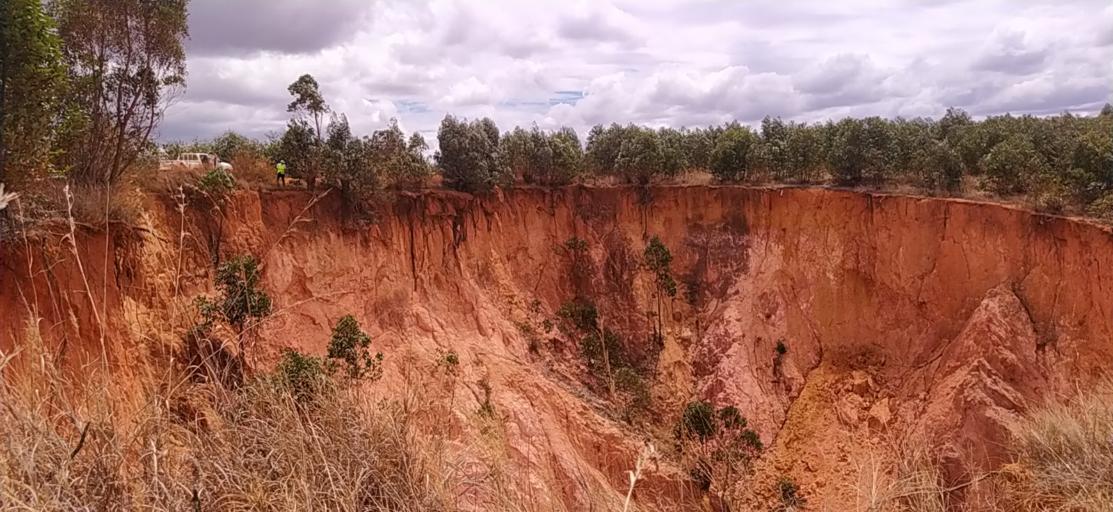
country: MG
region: Alaotra Mangoro
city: Ambatondrazaka
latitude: -18.0644
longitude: 48.2577
